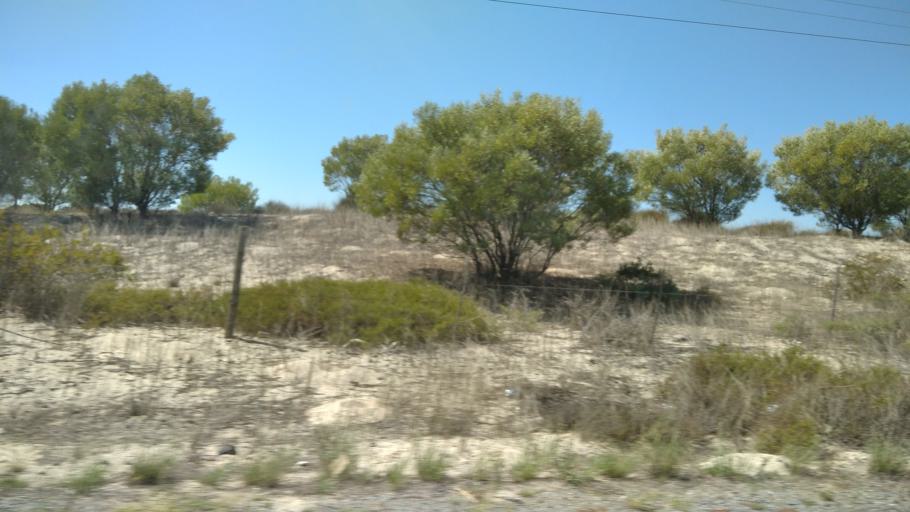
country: ZA
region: Western Cape
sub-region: West Coast District Municipality
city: Vredenburg
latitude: -33.0292
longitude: 18.2847
